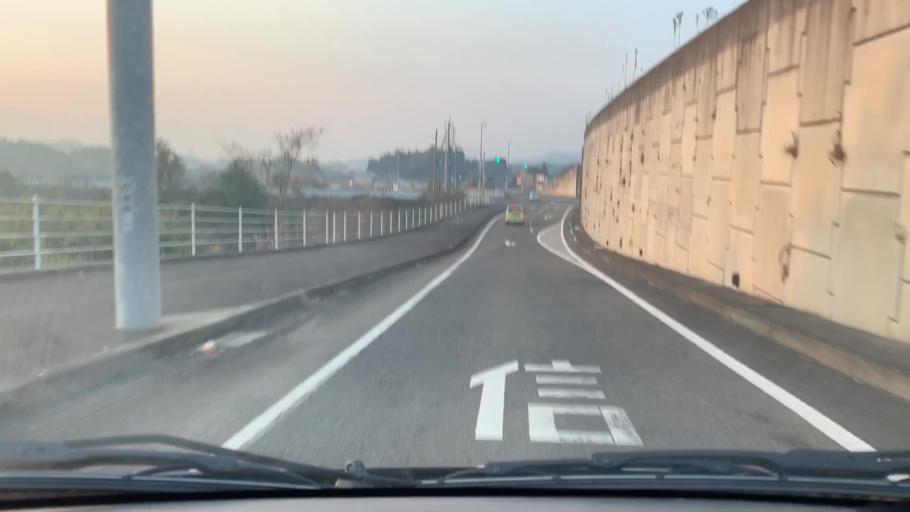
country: JP
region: Saga Prefecture
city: Imaricho-ko
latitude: 33.2638
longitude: 129.9084
